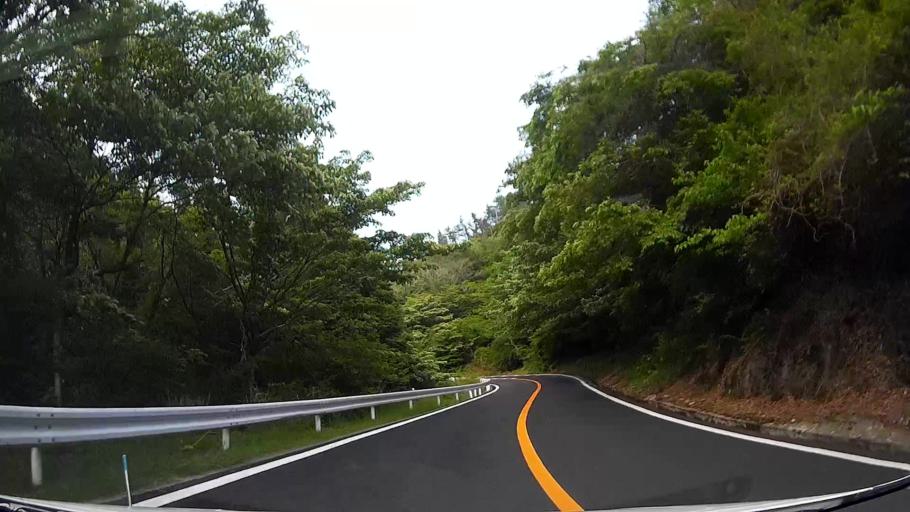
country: JP
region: Shizuoka
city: Ito
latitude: 34.9776
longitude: 139.0530
